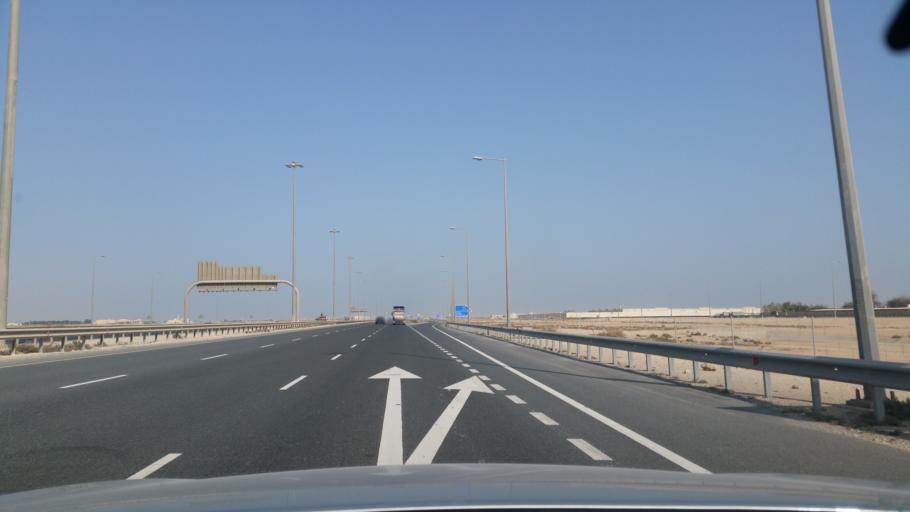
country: QA
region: Baladiyat az Za`ayin
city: Az Za`ayin
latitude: 25.5671
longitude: 51.4247
